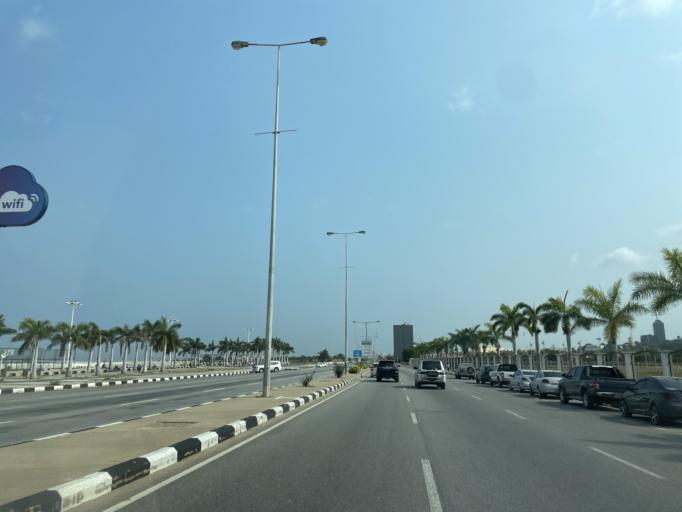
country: AO
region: Luanda
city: Luanda
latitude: -8.8243
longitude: 13.2158
